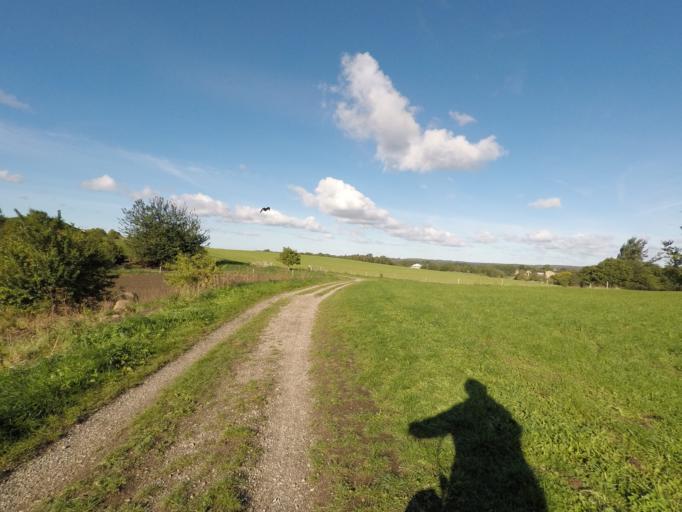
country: DK
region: Capital Region
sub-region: Ballerup Kommune
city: Malov
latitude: 55.7577
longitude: 12.3143
